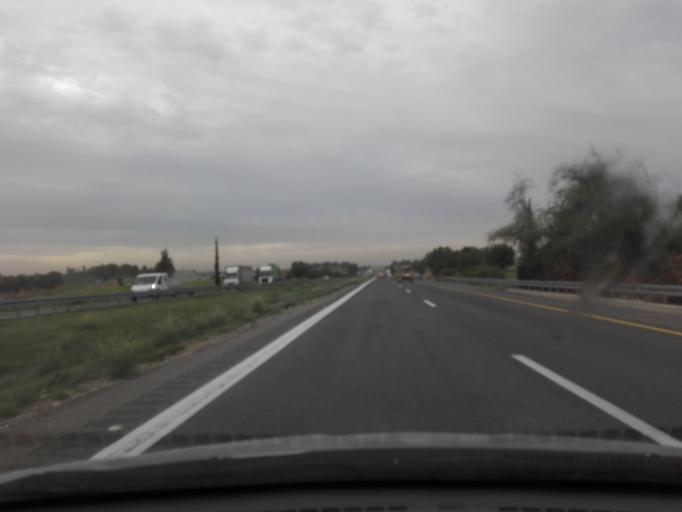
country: IL
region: Central District
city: Mazkeret Batya
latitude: 31.8495
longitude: 34.8683
